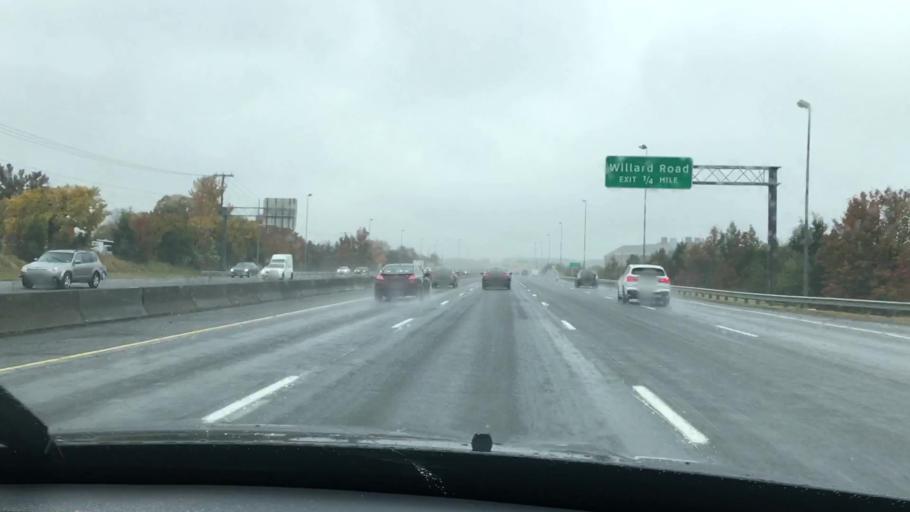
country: US
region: Virginia
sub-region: Fairfax County
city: Chantilly
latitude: 38.8928
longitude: -77.4426
